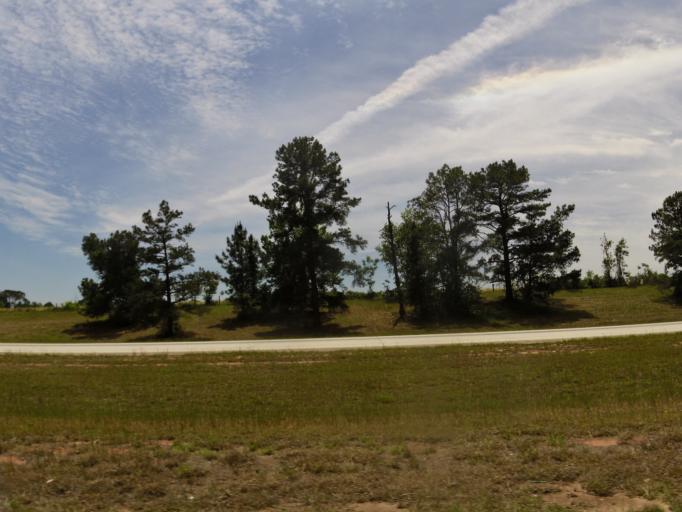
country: US
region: Georgia
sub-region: Evans County
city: Claxton
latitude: 32.3127
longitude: -81.8984
